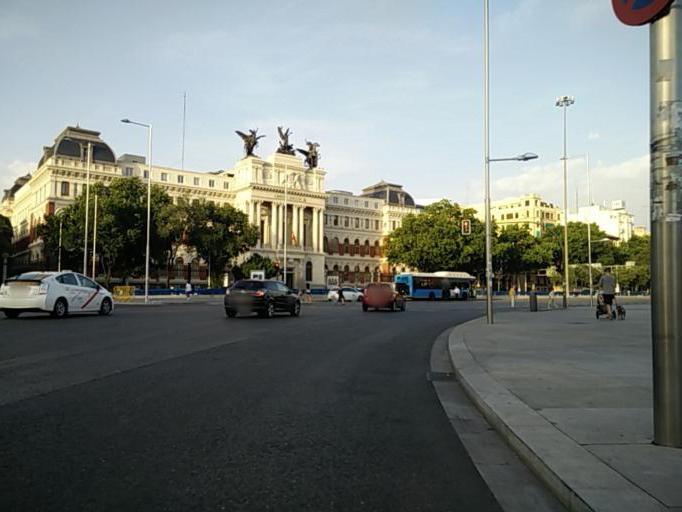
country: ES
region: Madrid
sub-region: Provincia de Madrid
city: Arganzuela
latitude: 40.4083
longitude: -3.6920
